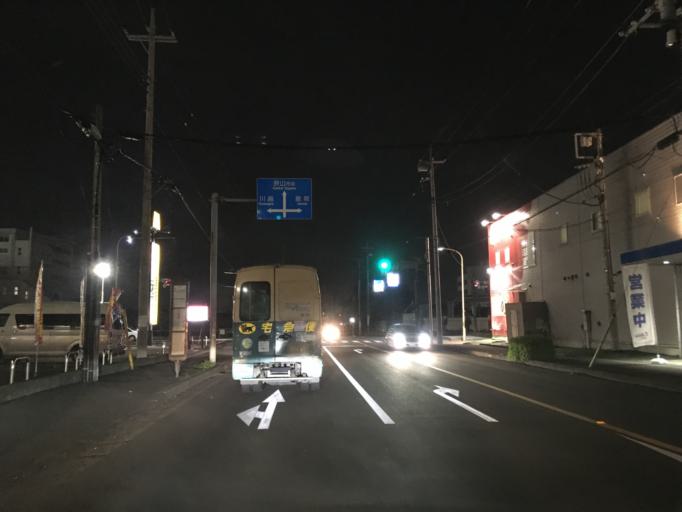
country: JP
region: Saitama
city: Sayama
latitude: 35.8746
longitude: 139.3907
